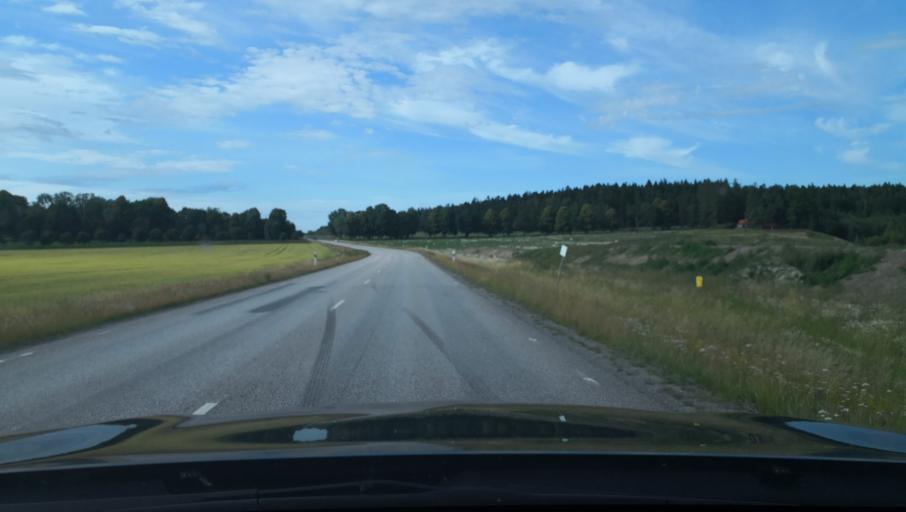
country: SE
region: Uppsala
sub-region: Habo Kommun
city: Balsta
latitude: 59.6129
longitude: 17.5003
